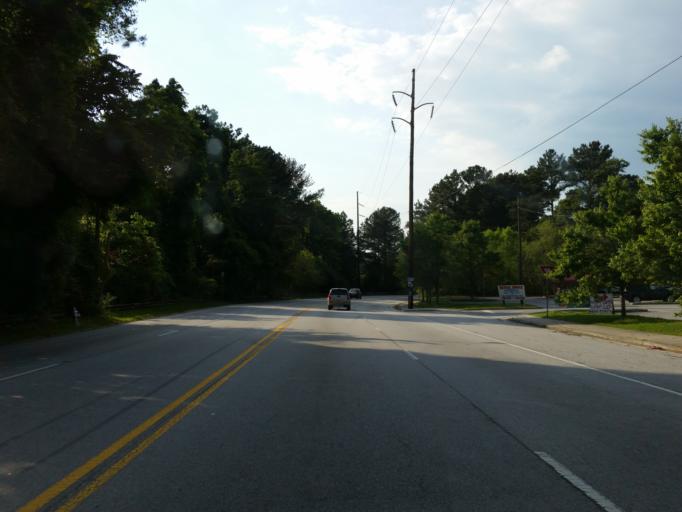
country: US
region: Georgia
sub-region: Cobb County
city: Vinings
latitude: 33.7789
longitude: -84.4753
